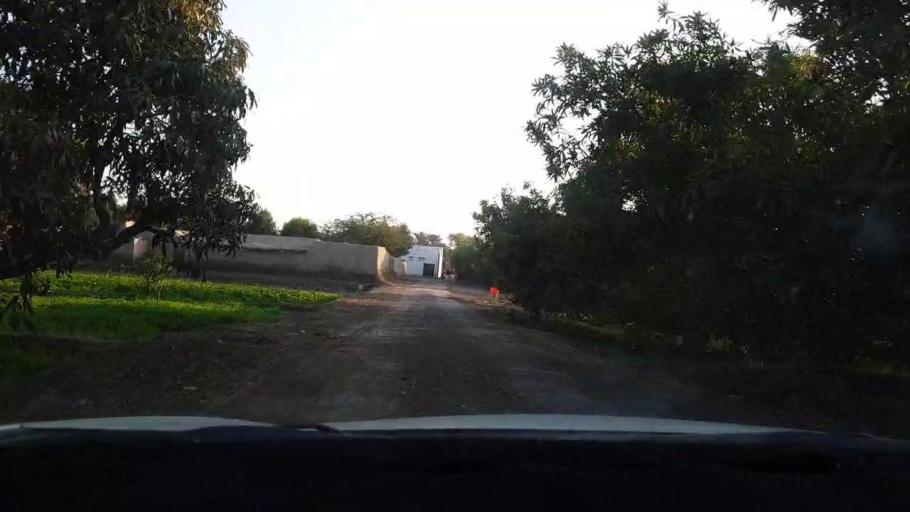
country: PK
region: Sindh
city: Berani
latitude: 25.7754
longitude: 68.7741
